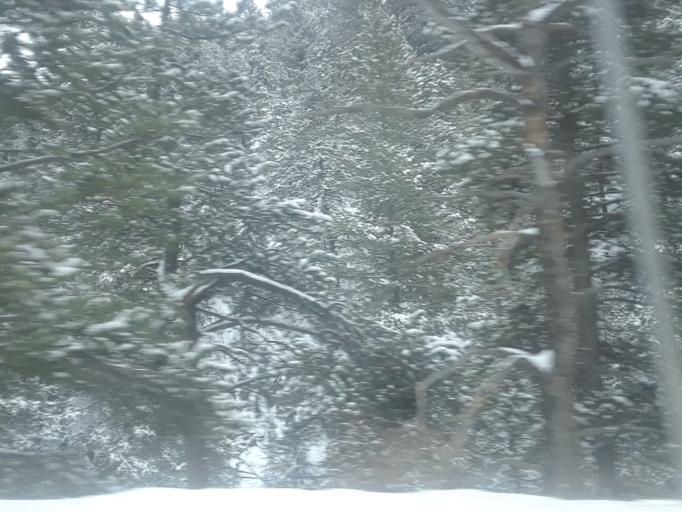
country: US
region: Colorado
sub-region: Boulder County
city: Coal Creek
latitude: 39.9275
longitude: -105.4229
